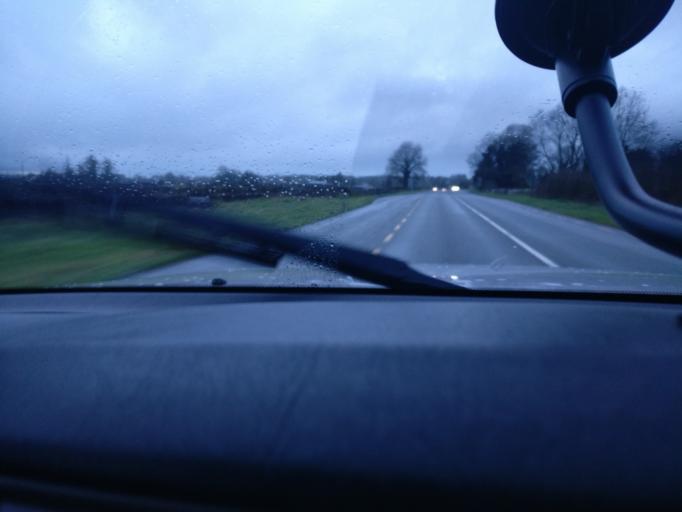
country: IE
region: Connaught
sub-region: County Galway
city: Ballinasloe
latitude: 53.2705
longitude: -8.3918
